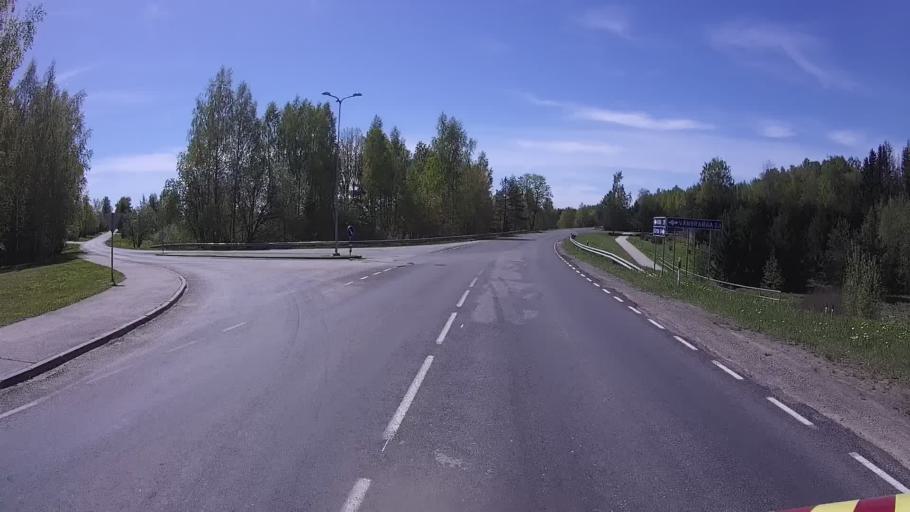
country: EE
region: Polvamaa
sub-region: Raepina vald
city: Rapina
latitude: 57.9941
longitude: 27.3344
